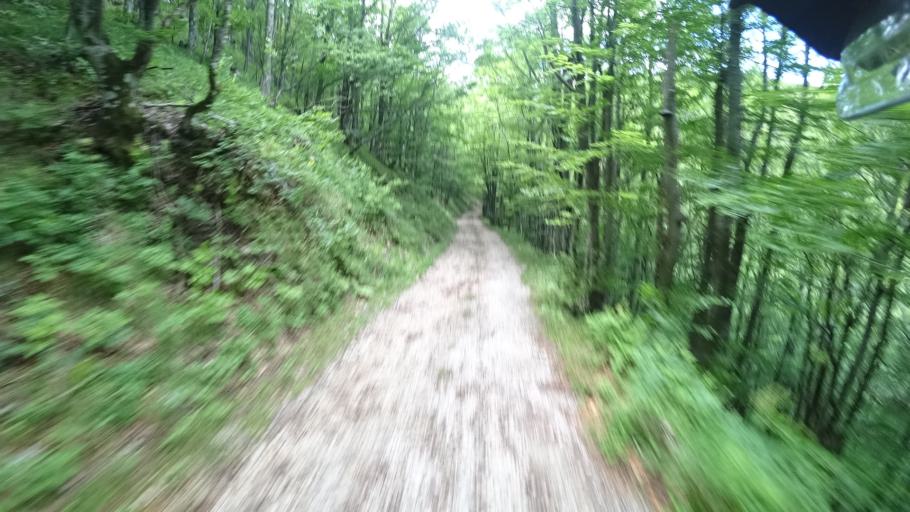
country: HR
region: Primorsko-Goranska
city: Bribir
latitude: 45.2387
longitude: 14.7742
